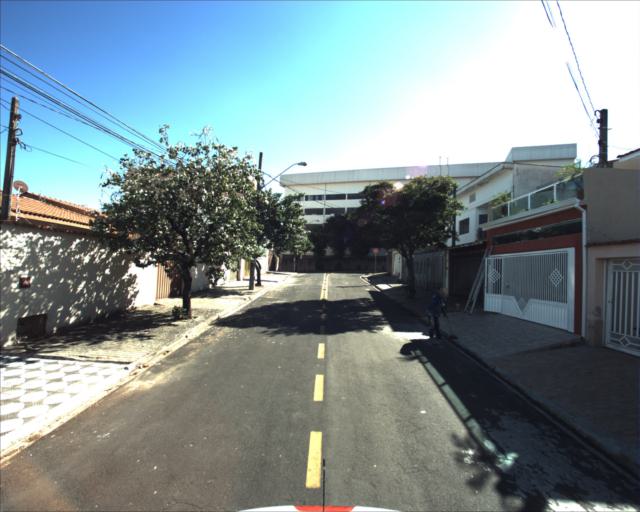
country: BR
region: Sao Paulo
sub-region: Sorocaba
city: Sorocaba
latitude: -23.4830
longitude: -47.4343
